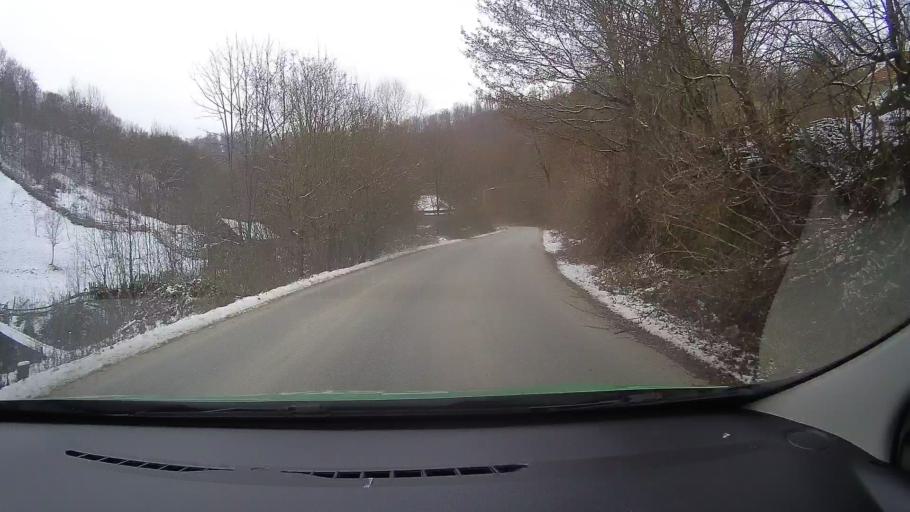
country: RO
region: Alba
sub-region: Oras Zlatna
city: Zlatna
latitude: 46.1111
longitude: 23.2047
